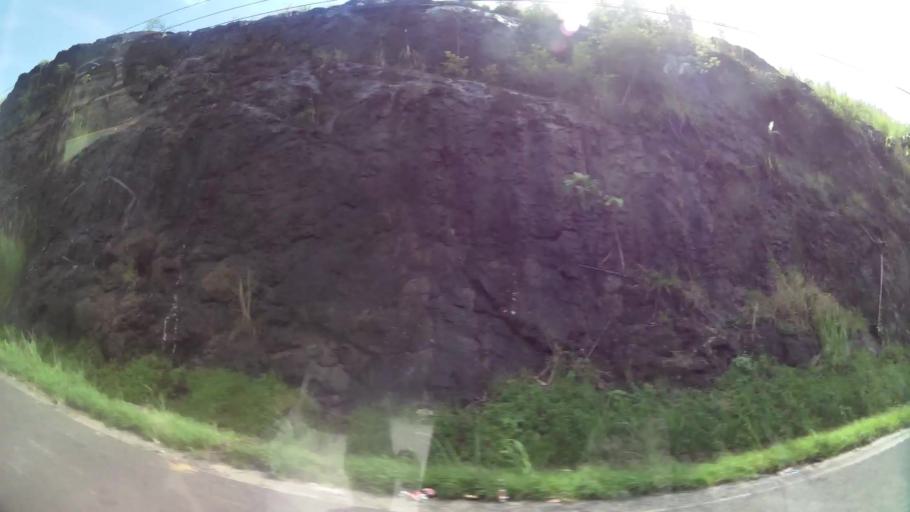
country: PA
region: Panama
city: Las Cumbres
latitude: 9.0411
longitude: -79.5652
